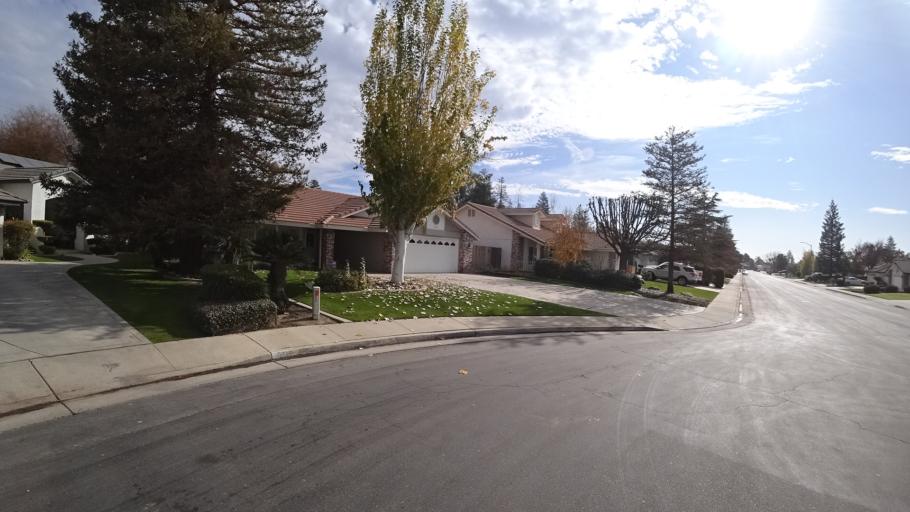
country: US
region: California
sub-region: Kern County
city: Greenacres
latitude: 35.4118
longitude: -119.1240
